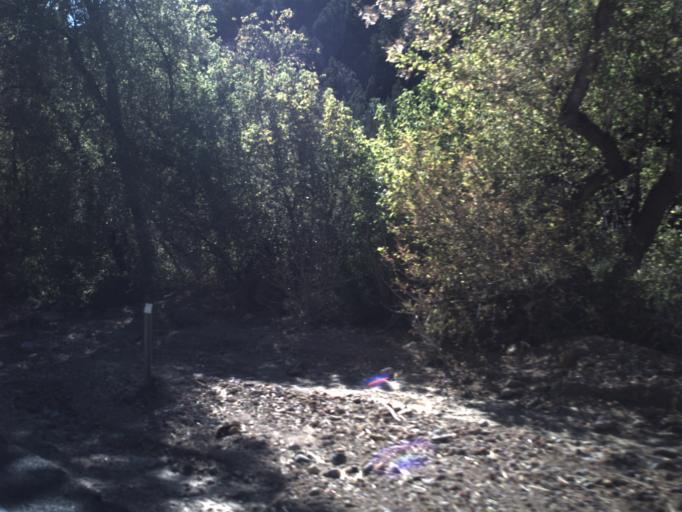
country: US
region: Utah
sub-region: Iron County
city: Parowan
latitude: 37.8004
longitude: -112.8144
